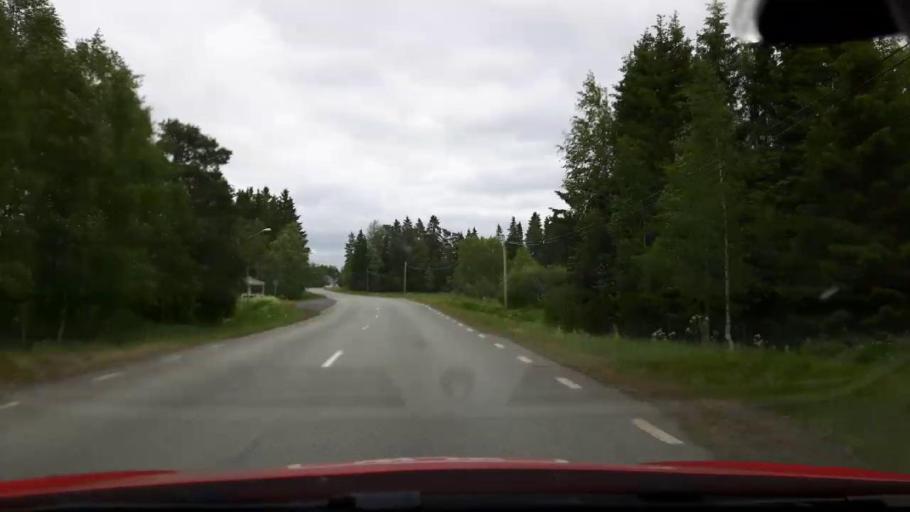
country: SE
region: Jaemtland
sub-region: OEstersunds Kommun
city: Lit
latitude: 63.6712
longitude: 15.0846
